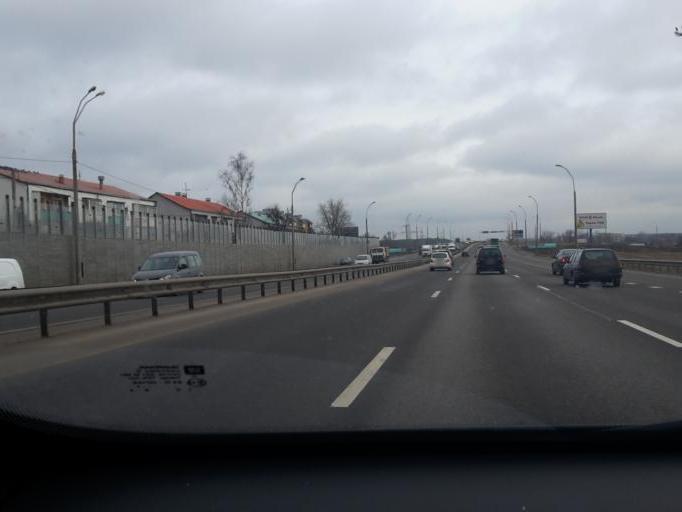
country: BY
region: Minsk
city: Zhdanovichy
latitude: 53.9383
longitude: 27.4295
